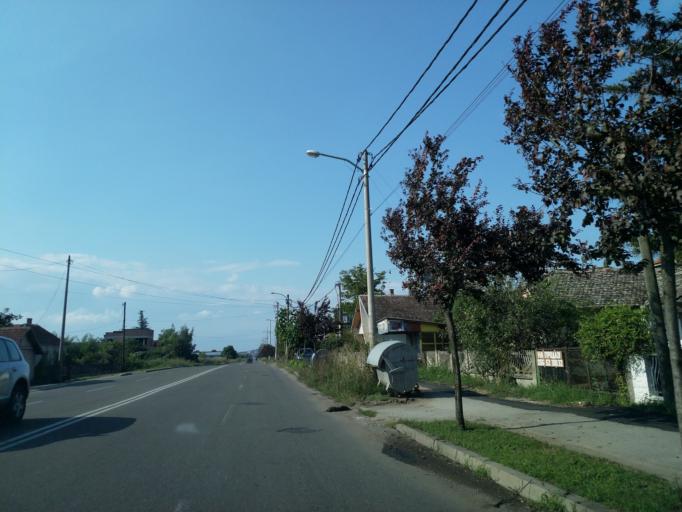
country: RS
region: Central Serbia
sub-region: Pomoravski Okrug
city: Paracin
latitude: 43.8332
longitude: 21.4165
